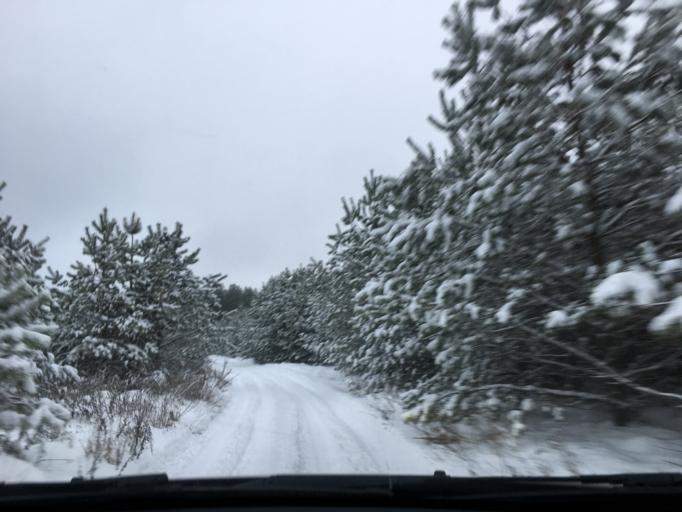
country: LT
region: Alytaus apskritis
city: Druskininkai
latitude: 53.9201
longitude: 24.1944
